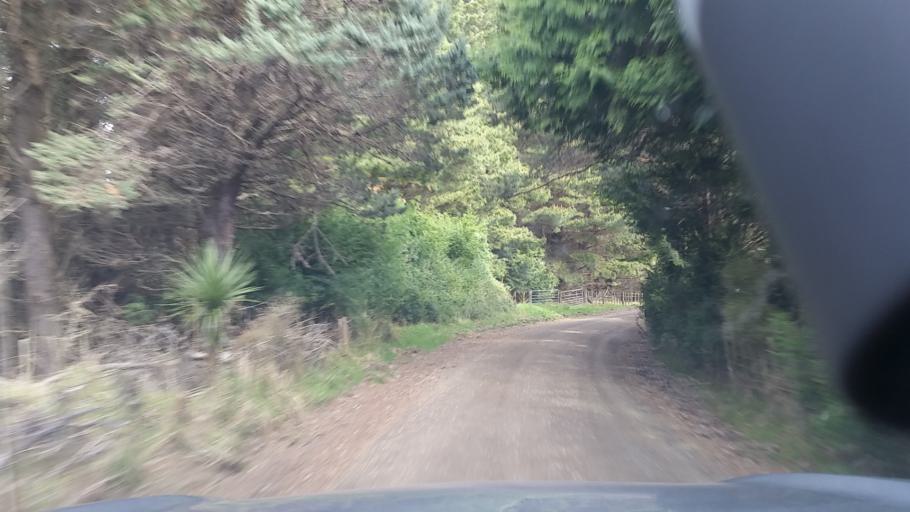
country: NZ
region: Hawke's Bay
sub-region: Napier City
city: Napier
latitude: -39.2296
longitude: 176.9943
